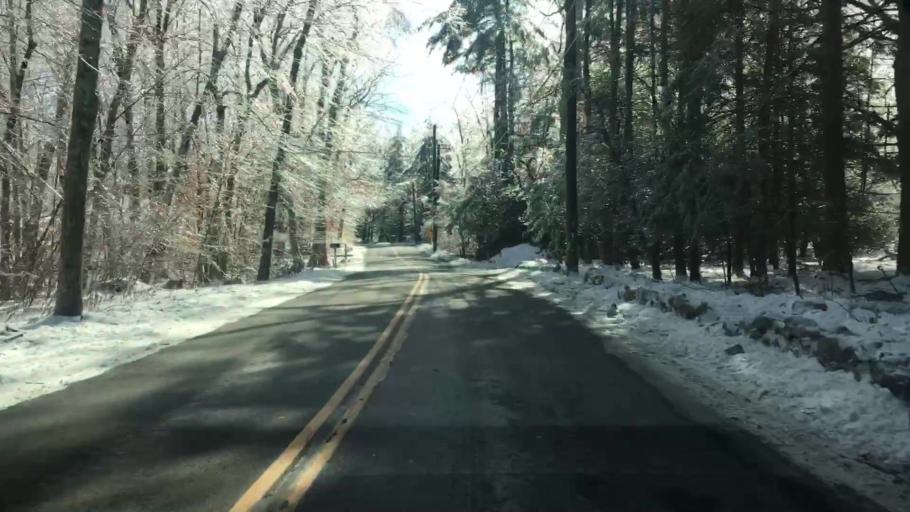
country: US
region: Connecticut
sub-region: Fairfield County
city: Newtown
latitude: 41.3491
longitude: -73.2326
